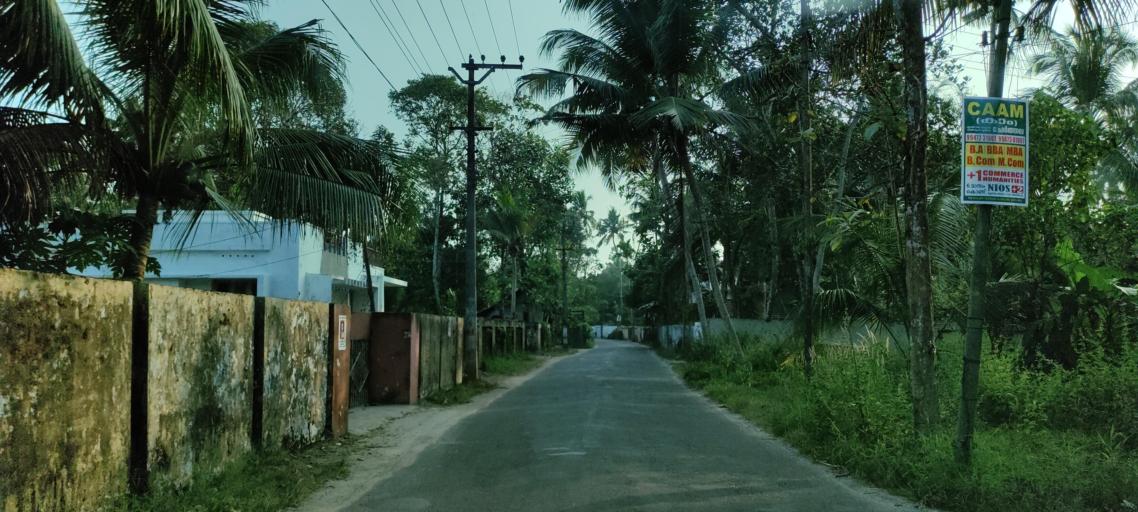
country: IN
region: Kerala
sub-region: Alappuzha
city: Shertallai
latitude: 9.6678
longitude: 76.3538
